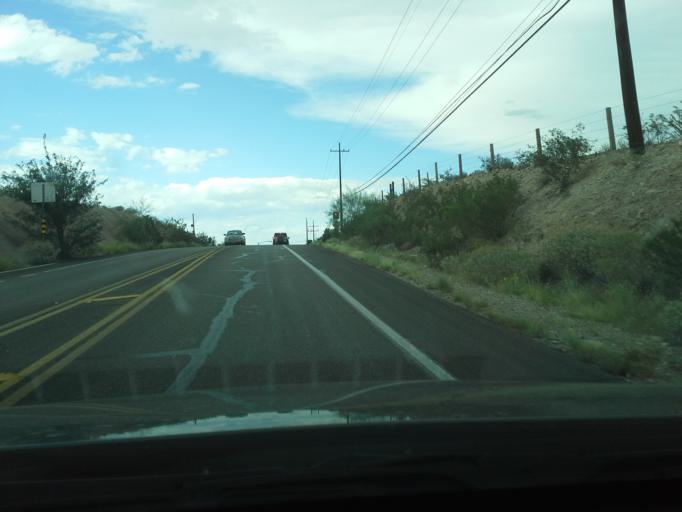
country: US
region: Arizona
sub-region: Pima County
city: South Tucson
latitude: 32.2228
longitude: -111.0203
